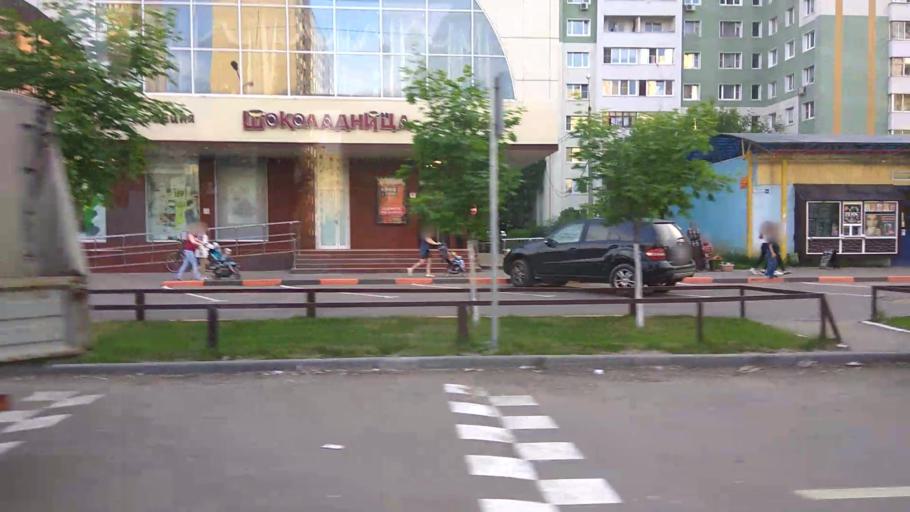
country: RU
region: Moskovskaya
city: Yubileyny
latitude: 55.9178
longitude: 37.8679
